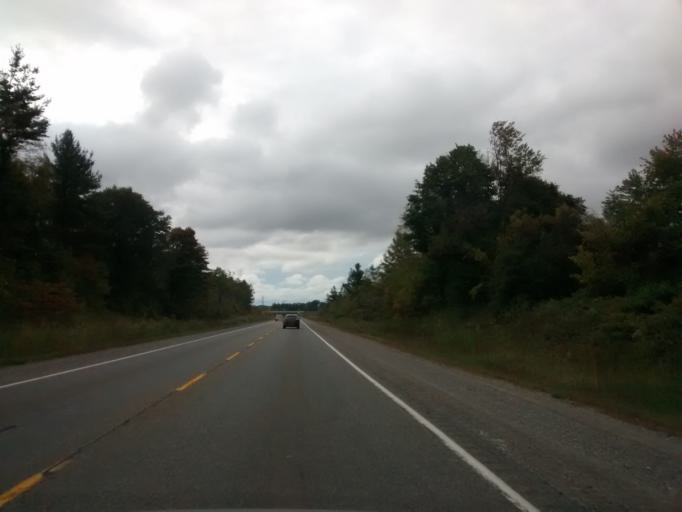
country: CA
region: Ontario
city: Ancaster
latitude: 43.1768
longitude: -79.9630
